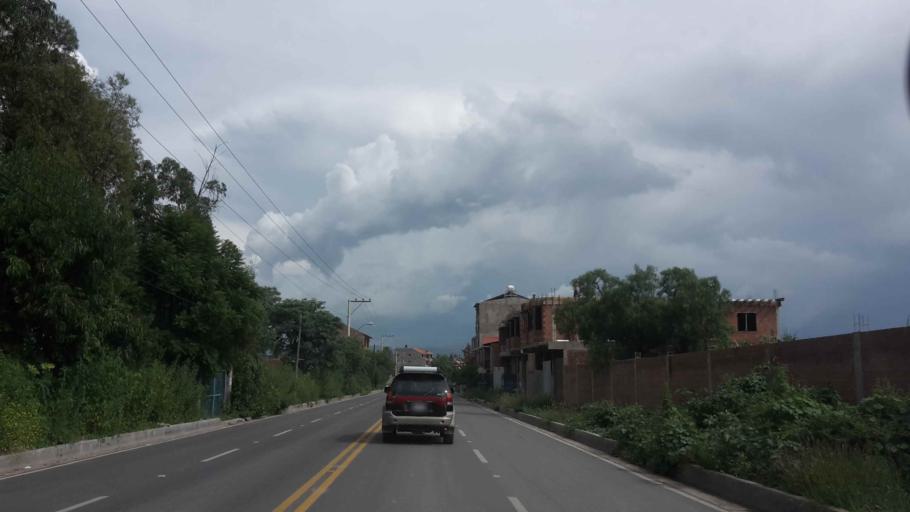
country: BO
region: Cochabamba
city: Cochabamba
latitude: -17.3507
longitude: -66.2565
